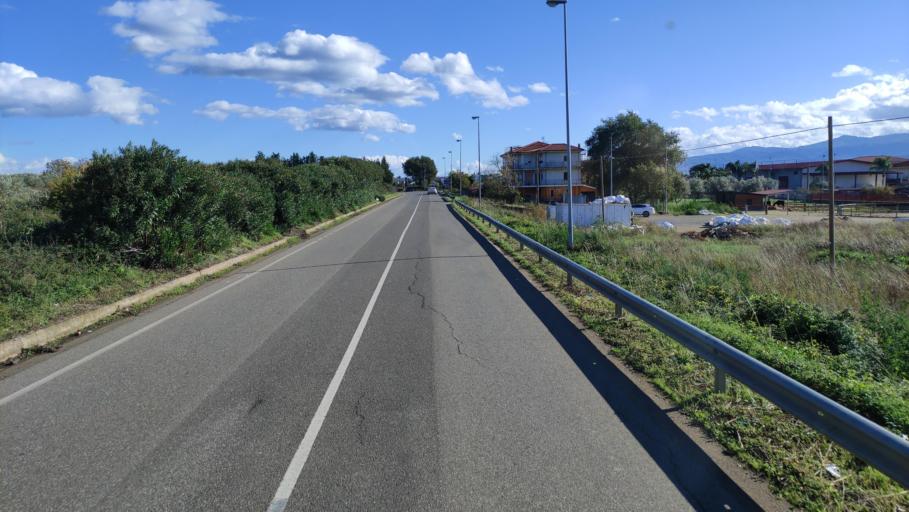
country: IT
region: Calabria
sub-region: Provincia di Catanzaro
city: Nicastro-Sambiase
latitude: 38.9369
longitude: 16.2850
